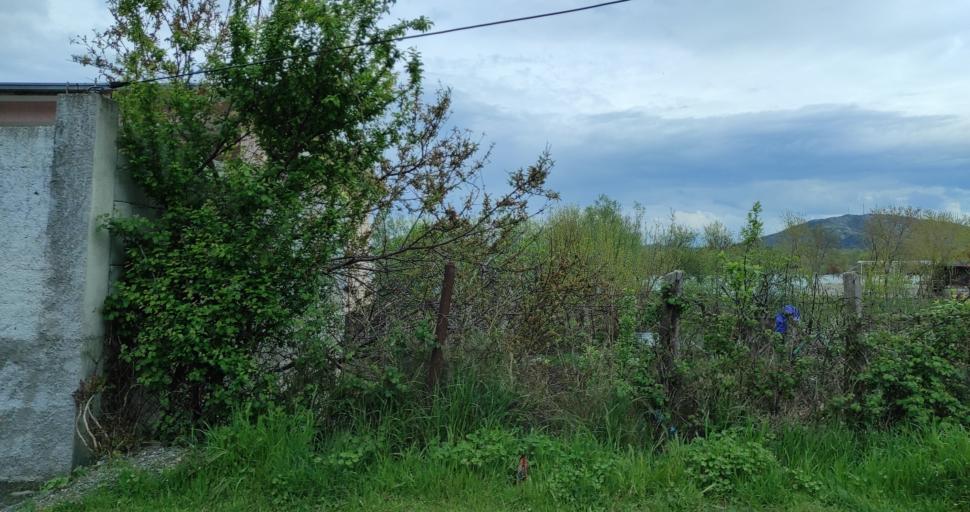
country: AL
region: Shkoder
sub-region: Rrethi i Shkodres
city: Berdica e Madhe
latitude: 42.0373
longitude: 19.4798
